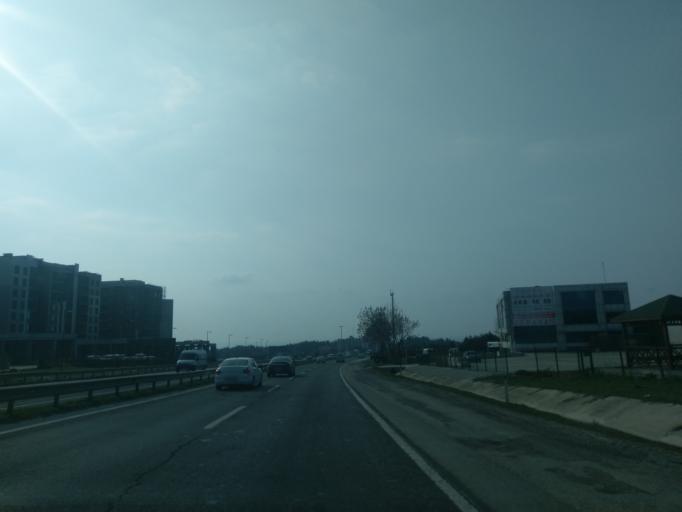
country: TR
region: Istanbul
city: Chekmejeh
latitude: 41.0074
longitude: 28.5150
